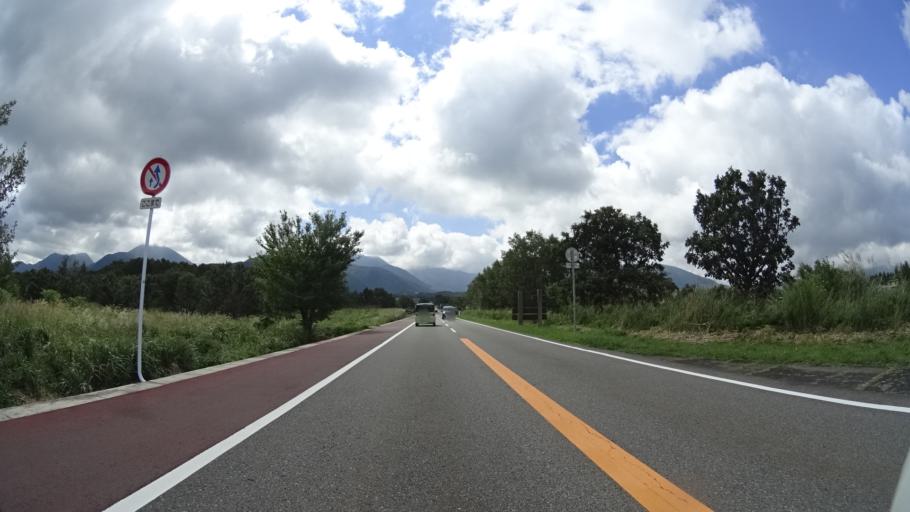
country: JP
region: Oita
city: Tsukawaki
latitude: 33.1554
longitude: 131.2410
